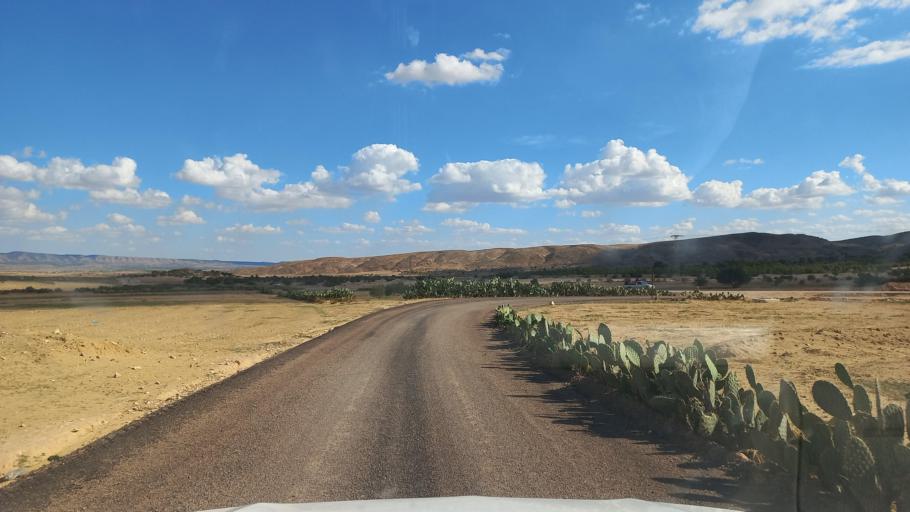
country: TN
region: Al Qasrayn
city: Sbiba
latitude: 35.4035
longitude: 8.9992
